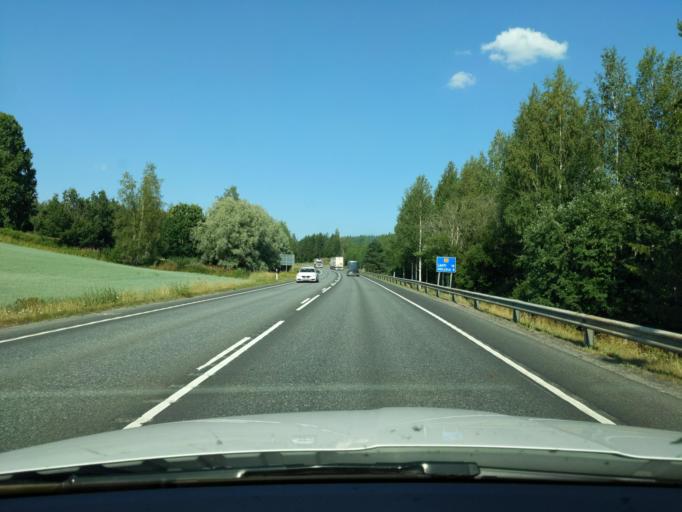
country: FI
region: Paijanne Tavastia
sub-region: Lahti
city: Hollola
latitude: 60.9508
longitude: 25.4277
